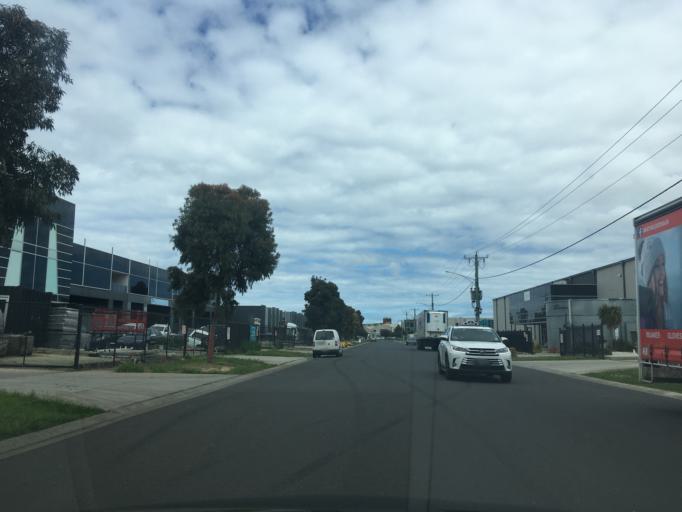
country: AU
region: Victoria
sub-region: Brimbank
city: Sunshine West
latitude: -37.8215
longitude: 144.8016
